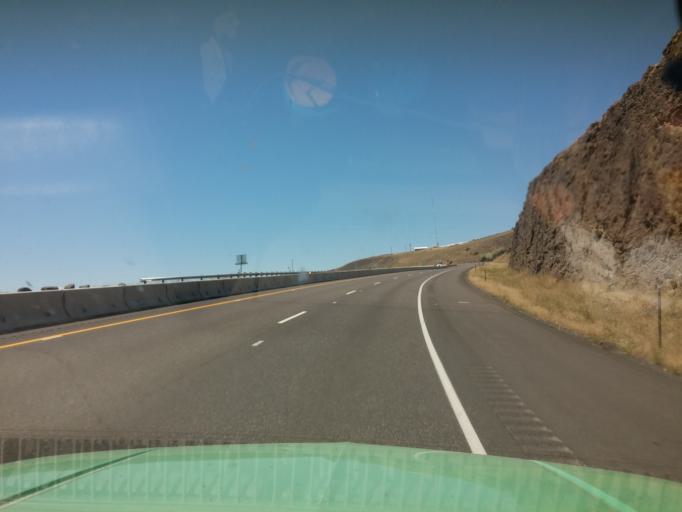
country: US
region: Idaho
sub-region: Nez Perce County
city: Lewiston
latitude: 46.4619
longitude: -116.9922
